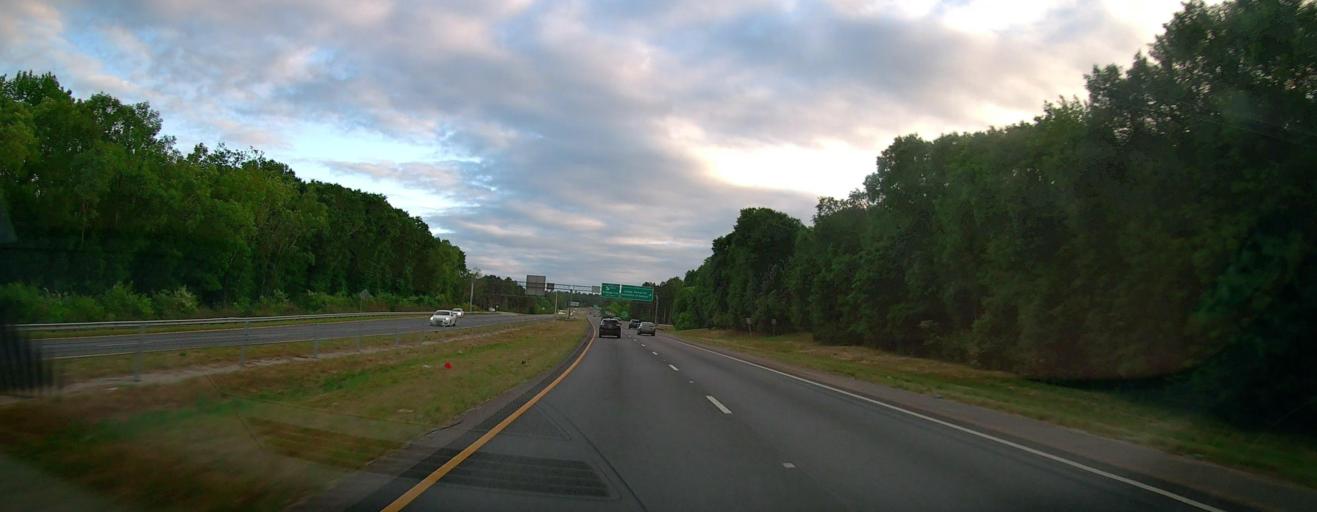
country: US
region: Georgia
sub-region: Clarke County
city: Athens
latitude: 33.9396
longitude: -83.3649
